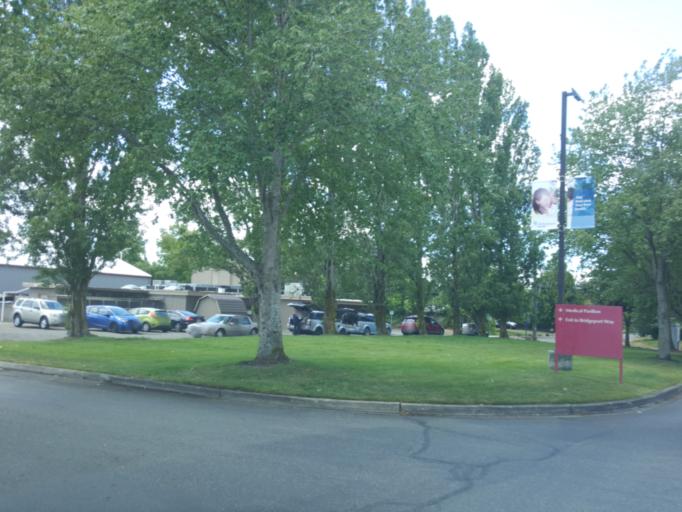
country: US
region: Washington
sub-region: Pierce County
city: McChord Air Force Base
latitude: 47.1538
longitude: -122.5033
